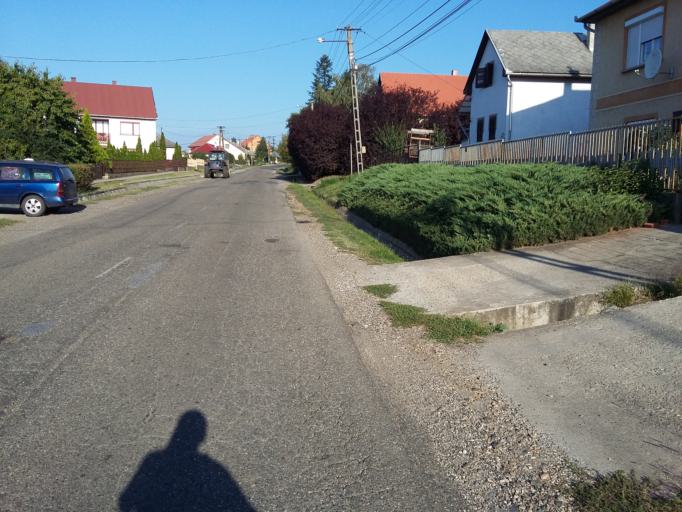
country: HU
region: Borsod-Abauj-Zemplen
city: Bekecs
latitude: 48.1527
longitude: 21.1661
